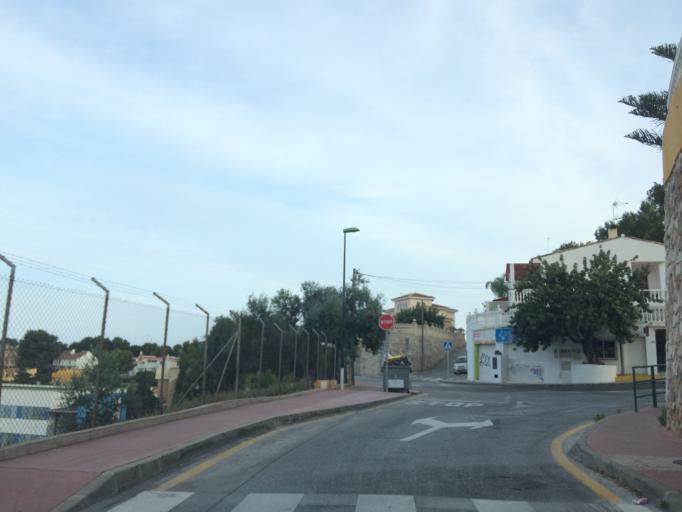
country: ES
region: Andalusia
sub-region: Provincia de Malaga
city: Malaga
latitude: 36.7274
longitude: -4.3855
